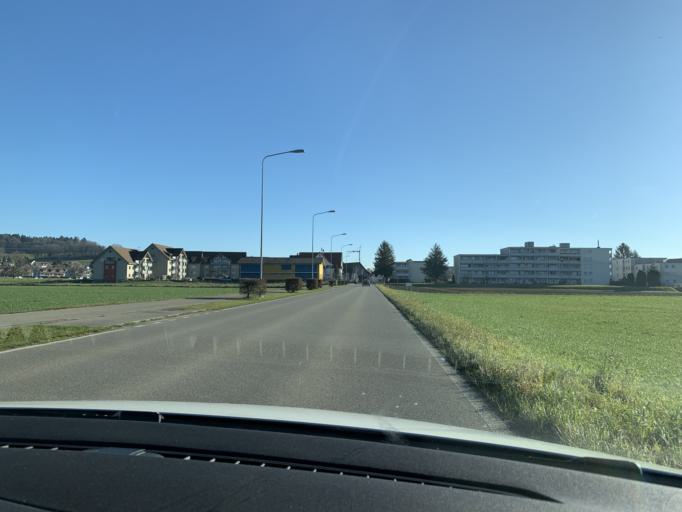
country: CH
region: Zurich
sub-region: Bezirk Dielsdorf
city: Regensdorf / Feldblumen-Riedthofstrasse
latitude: 47.4446
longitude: 8.4751
